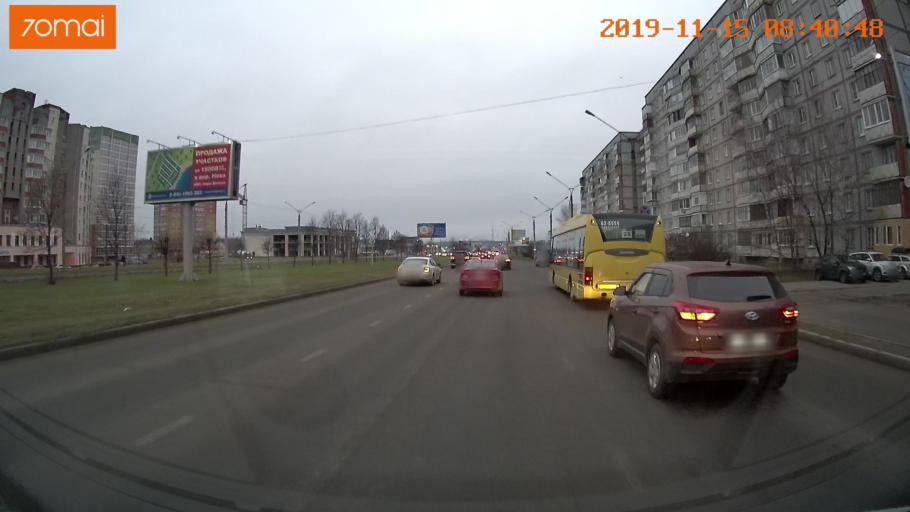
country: RU
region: Vologda
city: Cherepovets
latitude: 59.0958
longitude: 37.9132
